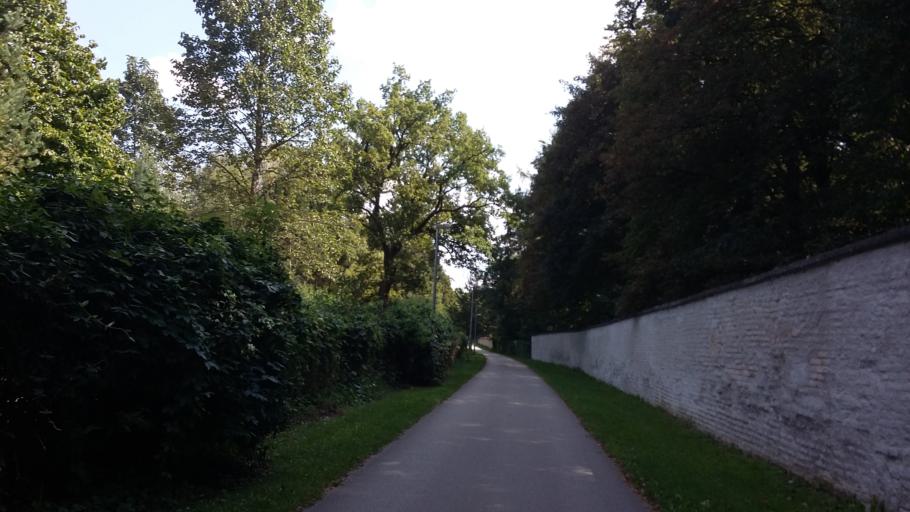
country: DE
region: Bavaria
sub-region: Upper Bavaria
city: Pasing
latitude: 48.1629
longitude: 11.4964
